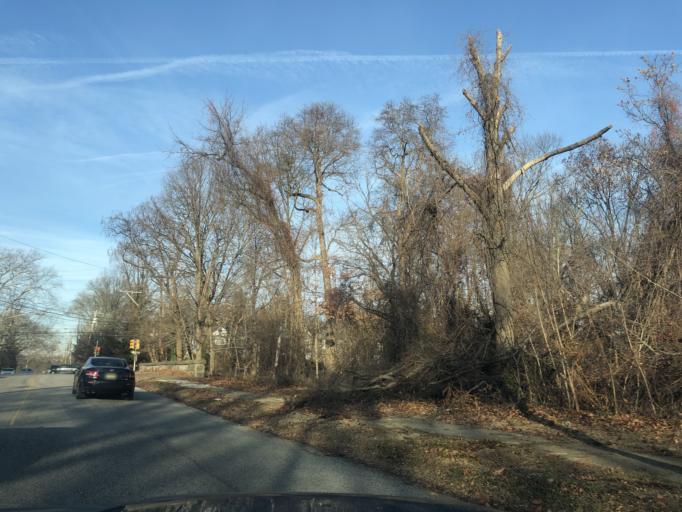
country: US
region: Pennsylvania
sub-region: Montgomery County
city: Bala-Cynwyd
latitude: 39.9900
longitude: -75.2194
